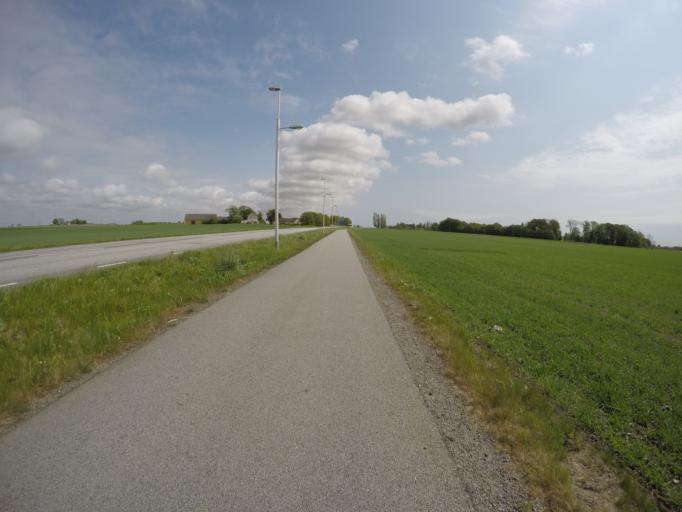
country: SE
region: Skane
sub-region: Malmo
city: Tygelsjo
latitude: 55.5333
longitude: 12.9917
